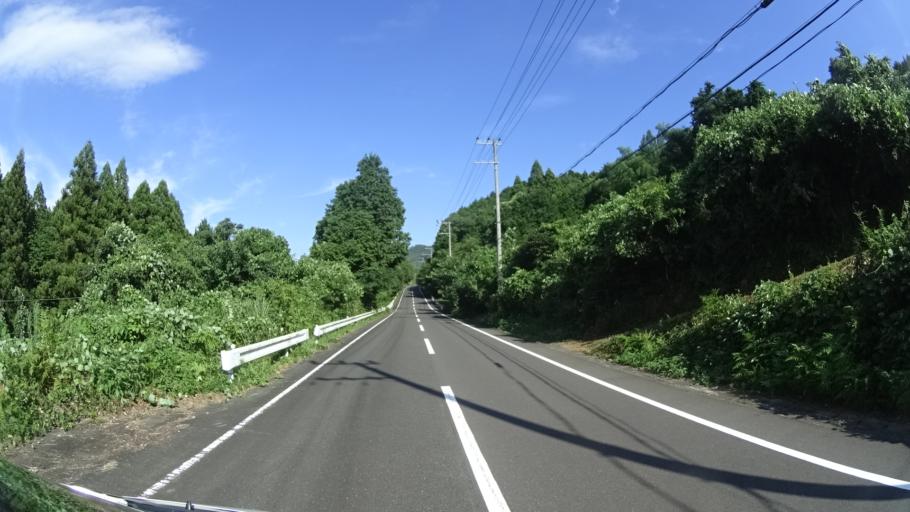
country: JP
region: Kyoto
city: Ayabe
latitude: 35.2869
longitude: 135.2846
